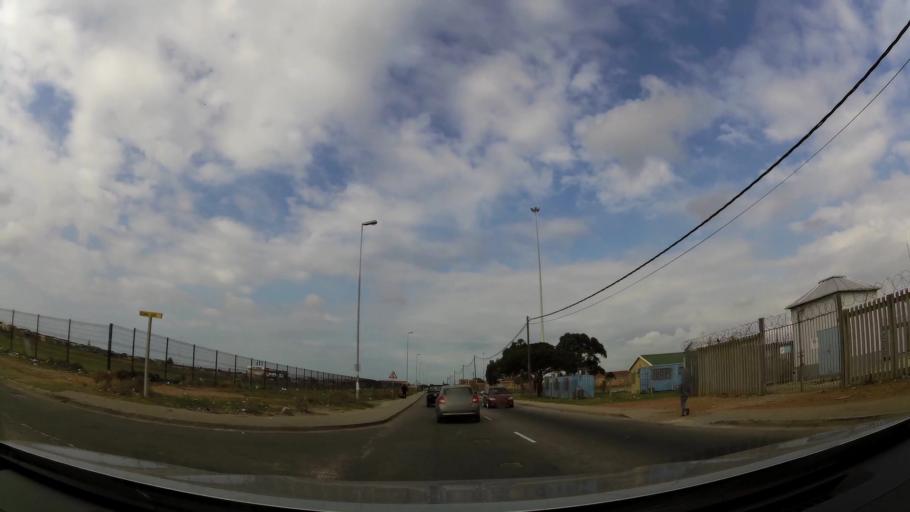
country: ZA
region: Eastern Cape
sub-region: Nelson Mandela Bay Metropolitan Municipality
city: Port Elizabeth
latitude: -33.8199
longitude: 25.5872
